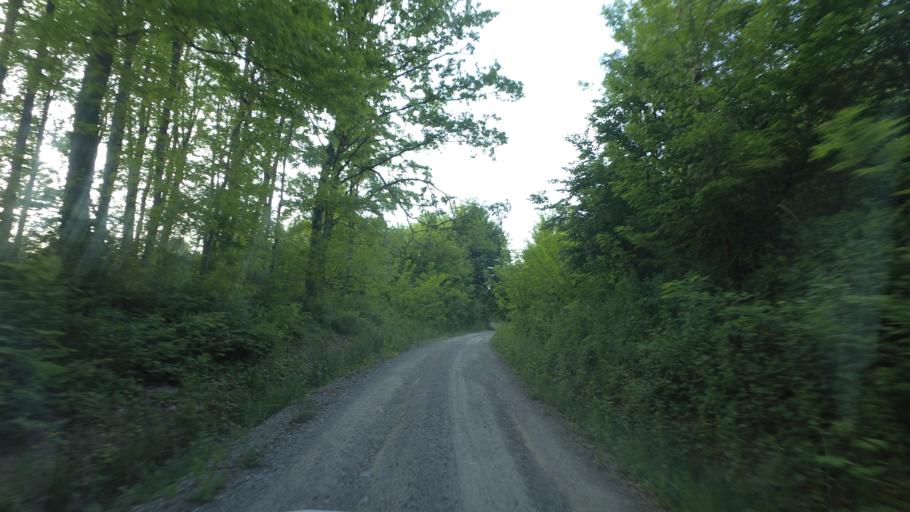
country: HR
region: Sisacko-Moslavacka
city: Gvozd
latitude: 45.3080
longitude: 15.9787
